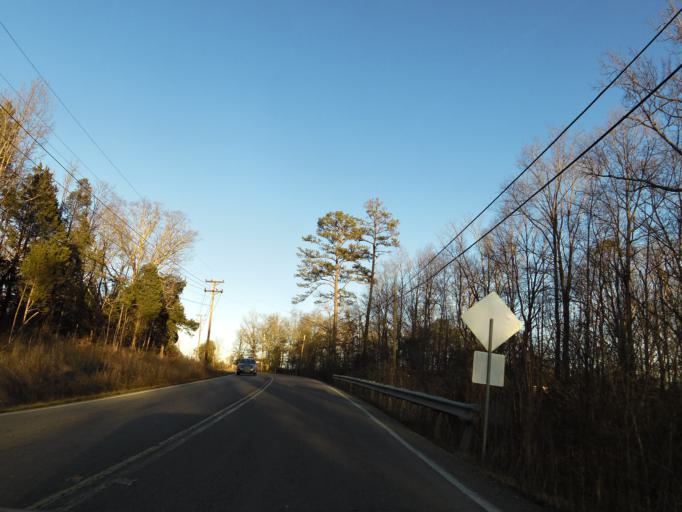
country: US
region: Tennessee
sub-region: Knox County
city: Mascot
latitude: 35.9806
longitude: -83.8139
